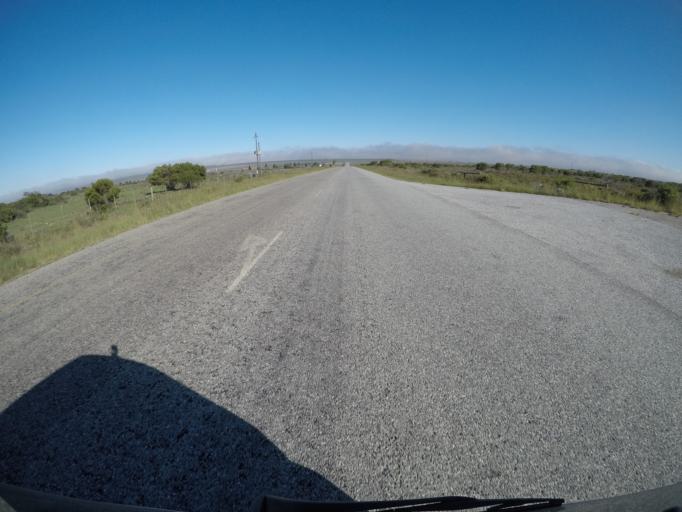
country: ZA
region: Western Cape
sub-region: Eden District Municipality
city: Mossel Bay
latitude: -34.1651
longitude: 22.0116
